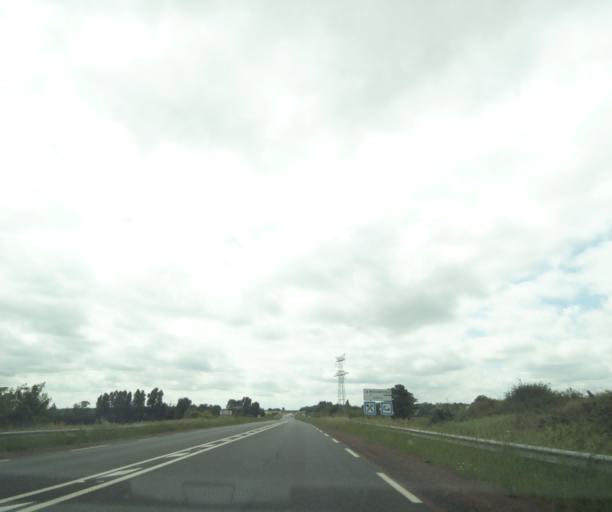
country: FR
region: Poitou-Charentes
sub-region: Departement des Deux-Sevres
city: Saint-Varent
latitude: 46.8364
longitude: -0.2077
